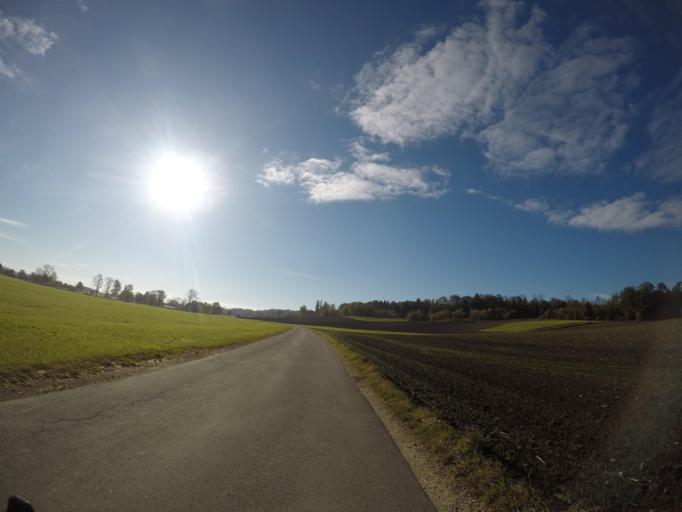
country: DE
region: Baden-Wuerttemberg
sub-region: Tuebingen Region
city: Saulgau
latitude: 48.0418
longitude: 9.4710
